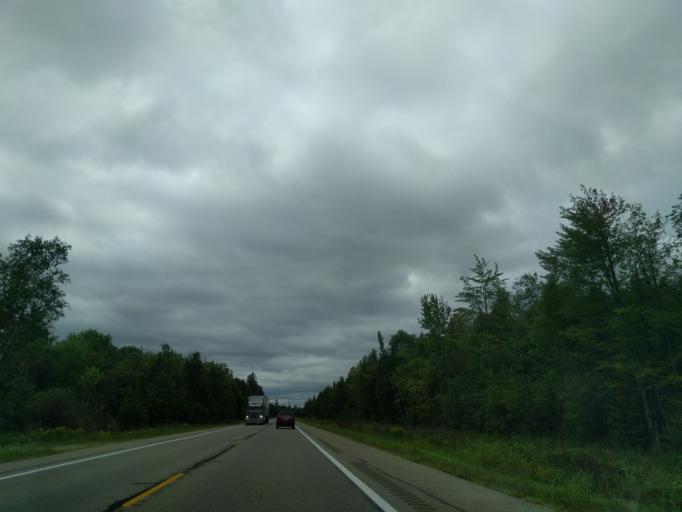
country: US
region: Michigan
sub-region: Delta County
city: Escanaba
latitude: 45.6046
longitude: -87.2226
